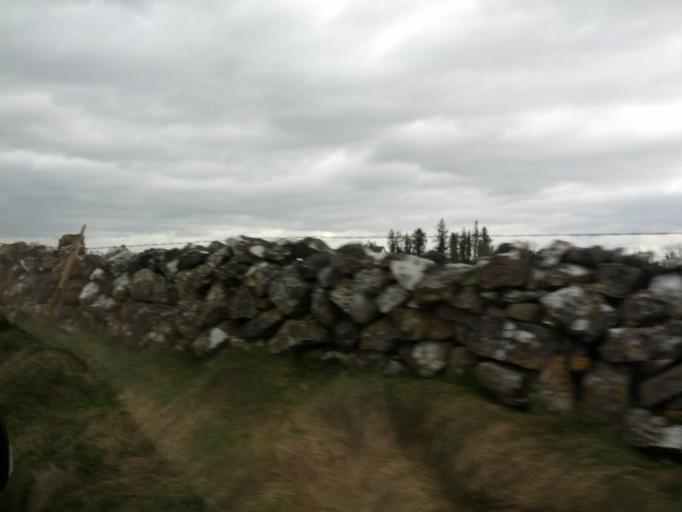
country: IE
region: Connaught
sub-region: County Galway
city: Athenry
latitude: 53.3997
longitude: -8.6396
